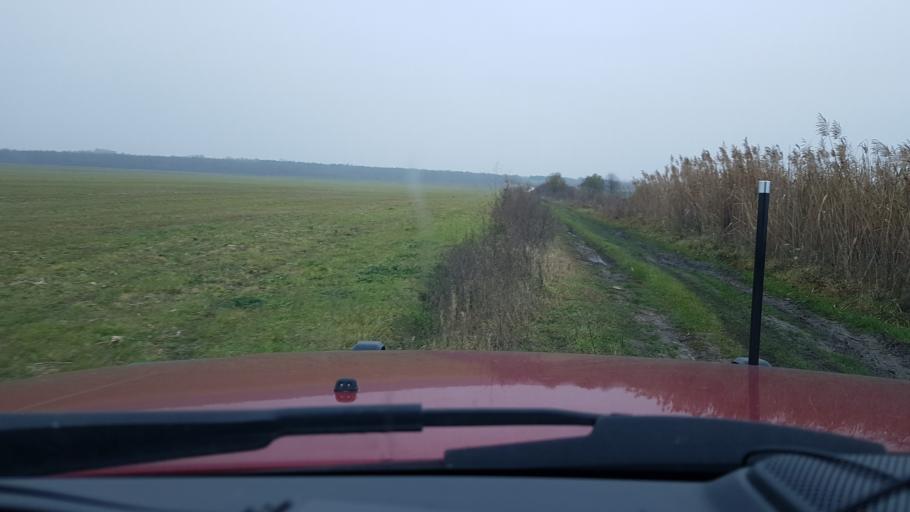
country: HU
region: Pest
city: Felsopakony
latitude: 47.3295
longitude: 19.2835
